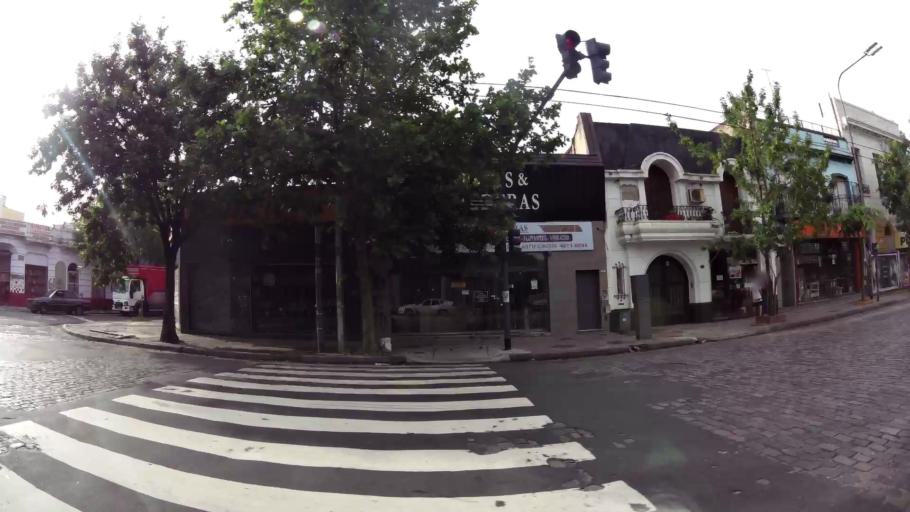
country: AR
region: Buenos Aires F.D.
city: Villa Santa Rita
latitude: -34.6384
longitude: -58.4815
